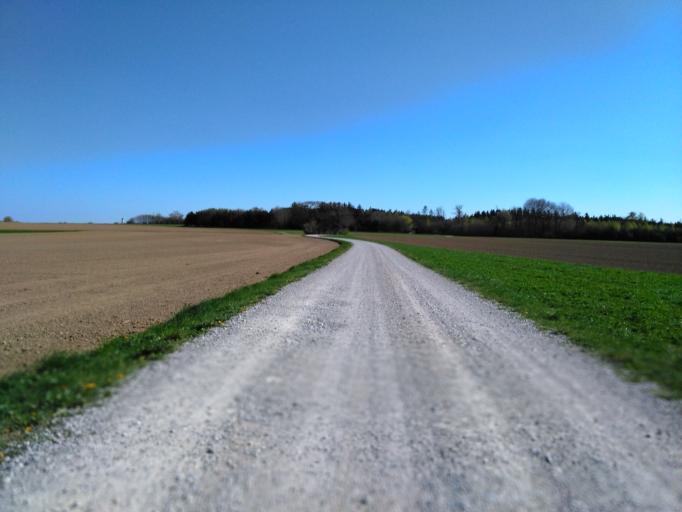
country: DE
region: Bavaria
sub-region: Upper Bavaria
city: Landsberied
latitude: 48.2044
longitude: 11.2035
